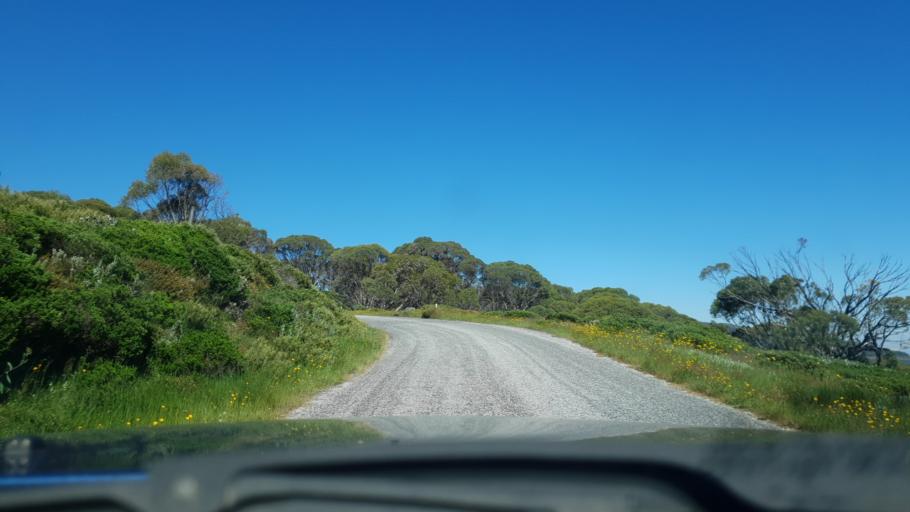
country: AU
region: Victoria
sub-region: Alpine
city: Mount Beauty
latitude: -36.8832
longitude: 147.3098
